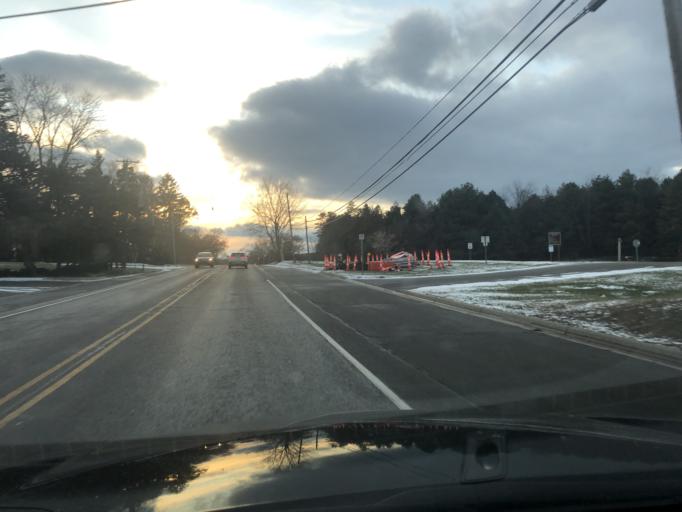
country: US
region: Michigan
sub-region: Oakland County
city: Milford
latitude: 42.5823
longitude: -83.6121
